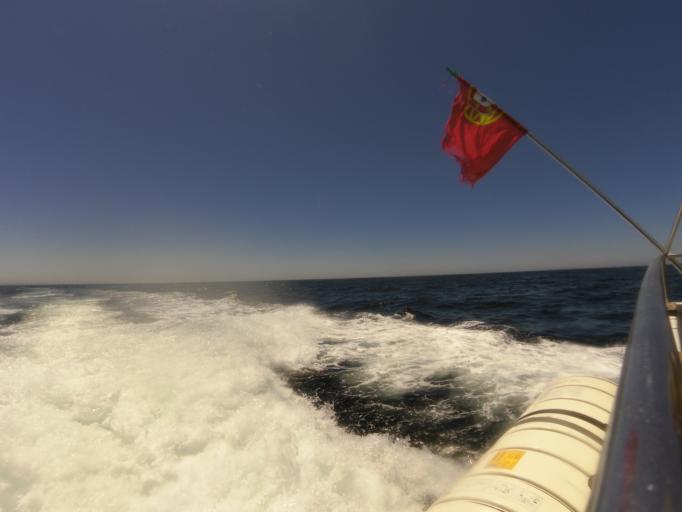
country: PT
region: Leiria
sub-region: Peniche
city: Peniche
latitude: 39.4080
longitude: -9.4986
